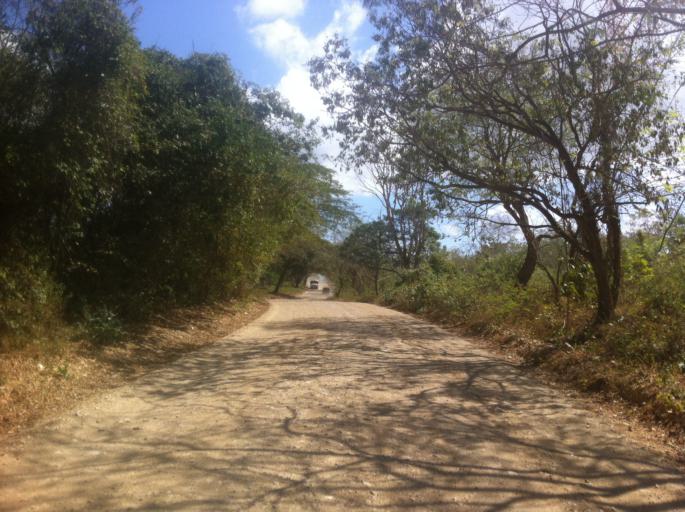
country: NI
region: Rivas
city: Tola
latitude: 11.4066
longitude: -86.0041
